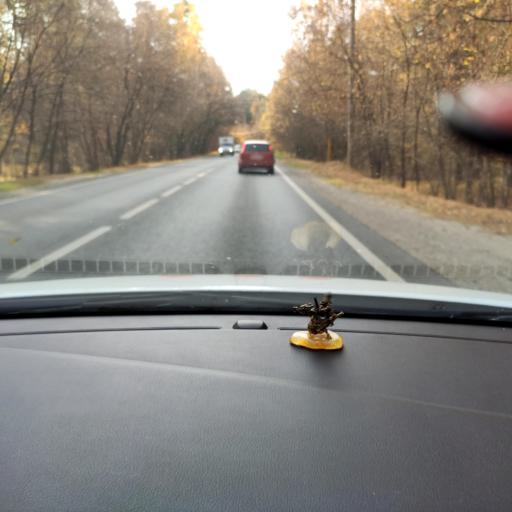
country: RU
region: Tatarstan
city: Osinovo
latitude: 55.8320
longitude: 48.8927
